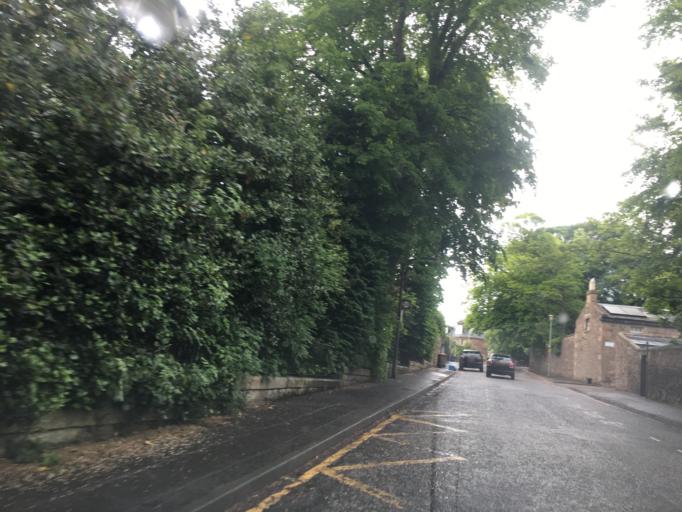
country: GB
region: Scotland
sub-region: Edinburgh
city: Edinburgh
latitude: 55.9301
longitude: -3.2151
